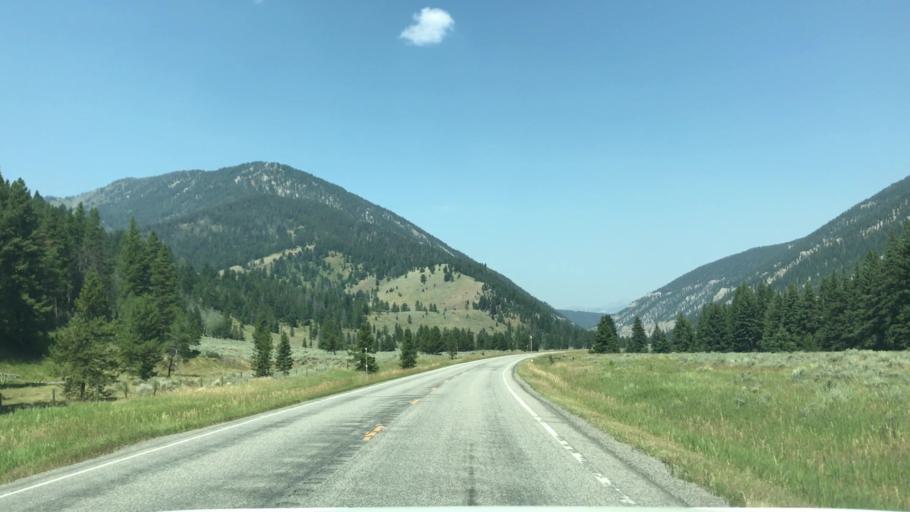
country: US
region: Montana
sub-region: Gallatin County
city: Big Sky
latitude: 45.1036
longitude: -111.2206
